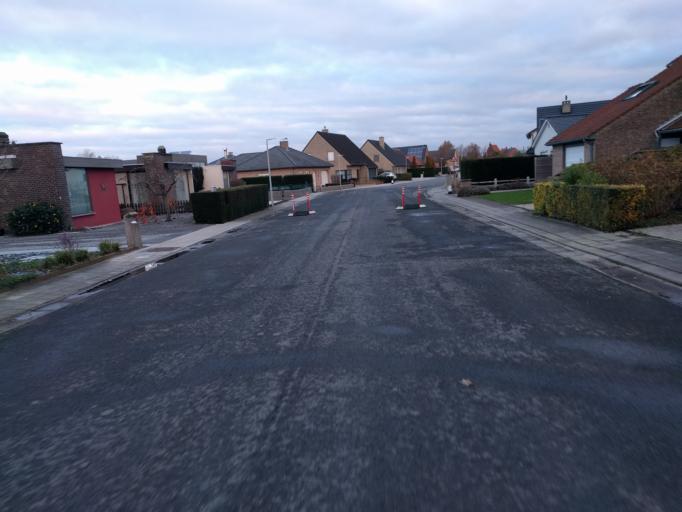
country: BE
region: Flanders
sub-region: Provincie West-Vlaanderen
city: Wevelgem
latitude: 50.8065
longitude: 3.1684
